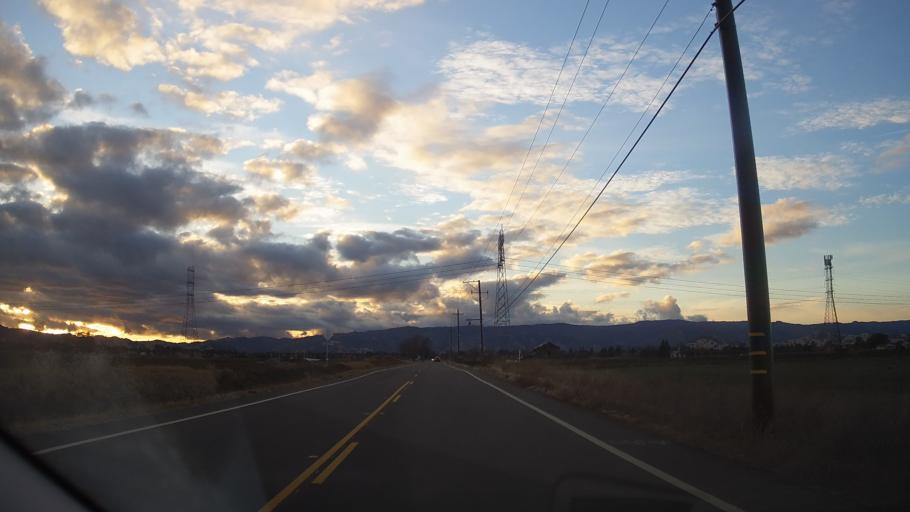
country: US
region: California
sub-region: Solano County
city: Hartley
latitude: 38.3590
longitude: -121.9166
